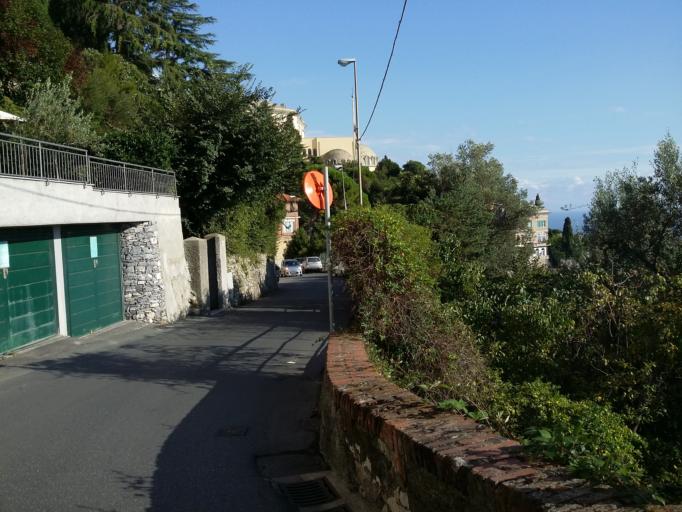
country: IT
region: Liguria
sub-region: Provincia di Genova
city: Genoa
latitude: 44.4218
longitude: 8.9367
